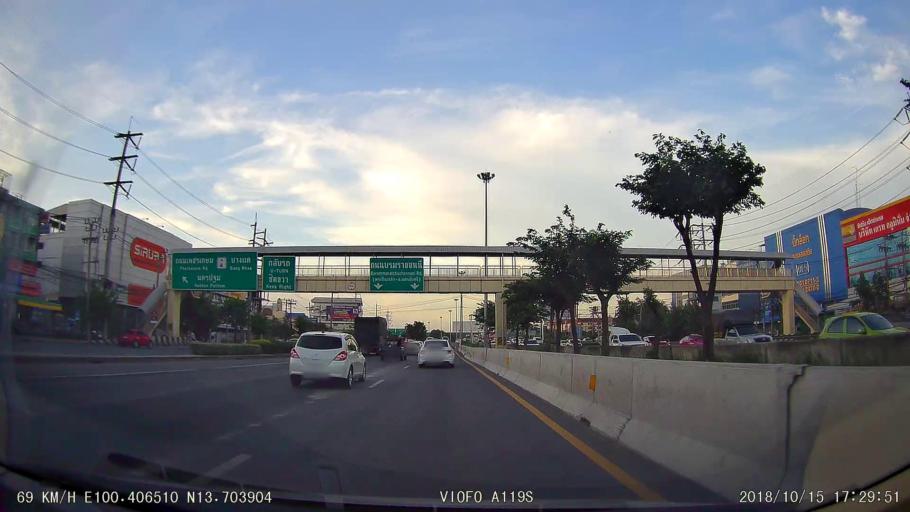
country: TH
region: Bangkok
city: Bang Khae
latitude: 13.7042
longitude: 100.4065
